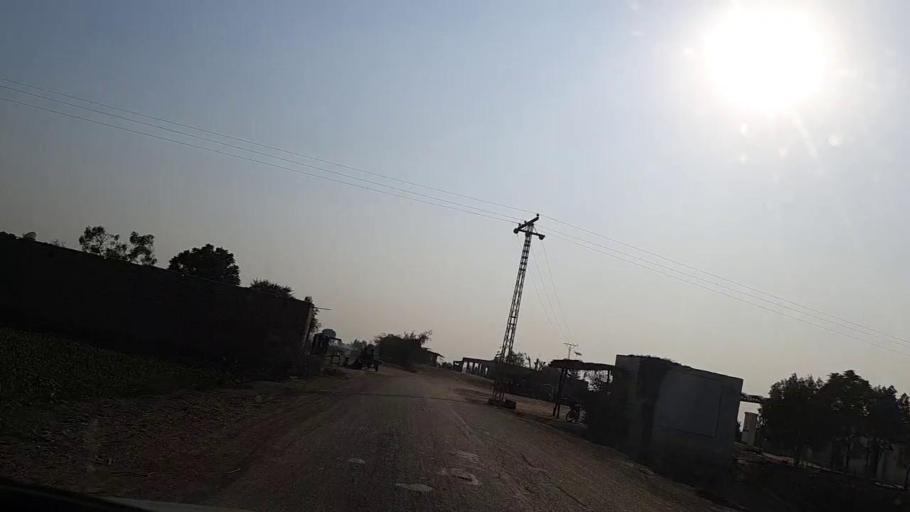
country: PK
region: Sindh
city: Sakrand
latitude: 26.0716
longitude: 68.2608
